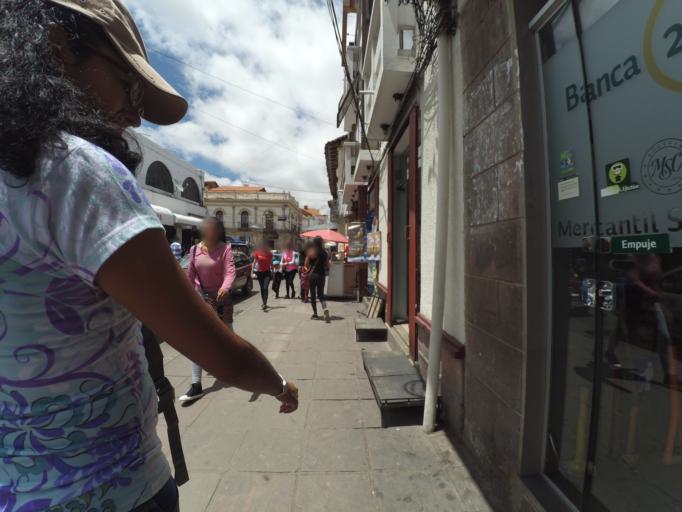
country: BO
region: Chuquisaca
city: Sucre
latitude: -19.0452
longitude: -65.2596
